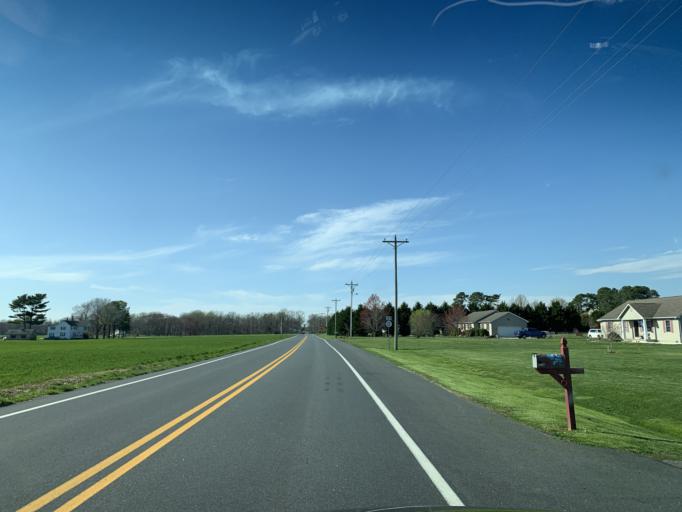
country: US
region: Delaware
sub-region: Kent County
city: Riverview
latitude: 39.0050
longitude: -75.5230
